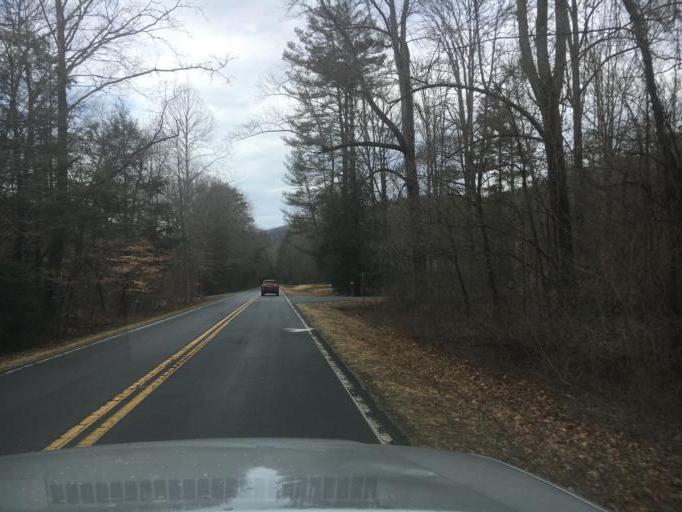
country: US
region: North Carolina
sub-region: Transylvania County
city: Brevard
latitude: 35.2839
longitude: -82.7249
